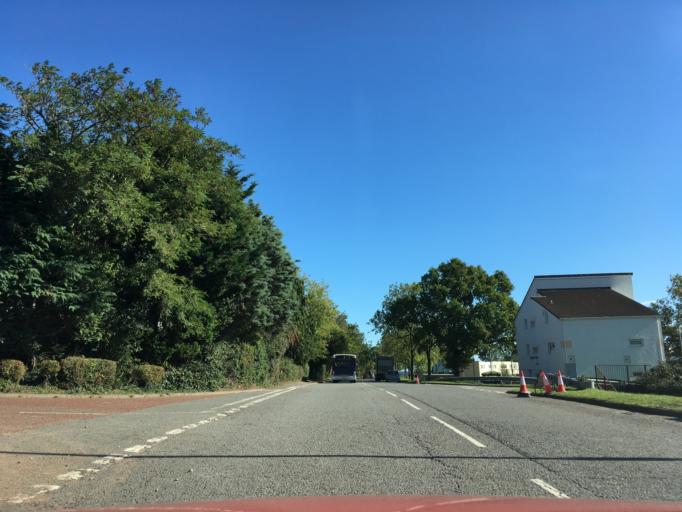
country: GB
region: Wales
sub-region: Torfaen County Borough
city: Cwmbran
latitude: 51.6502
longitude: -3.0372
